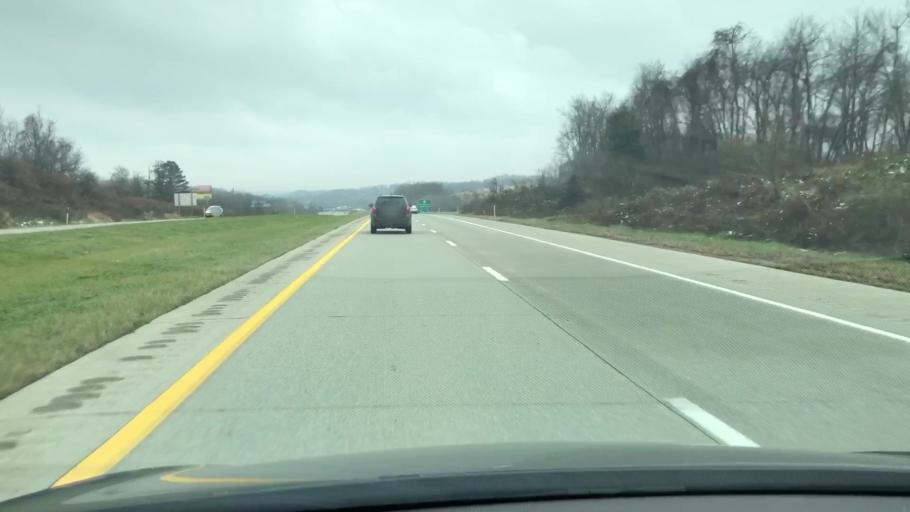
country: US
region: Pennsylvania
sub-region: Westmoreland County
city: Mount Pleasant
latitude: 40.1674
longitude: -79.5605
